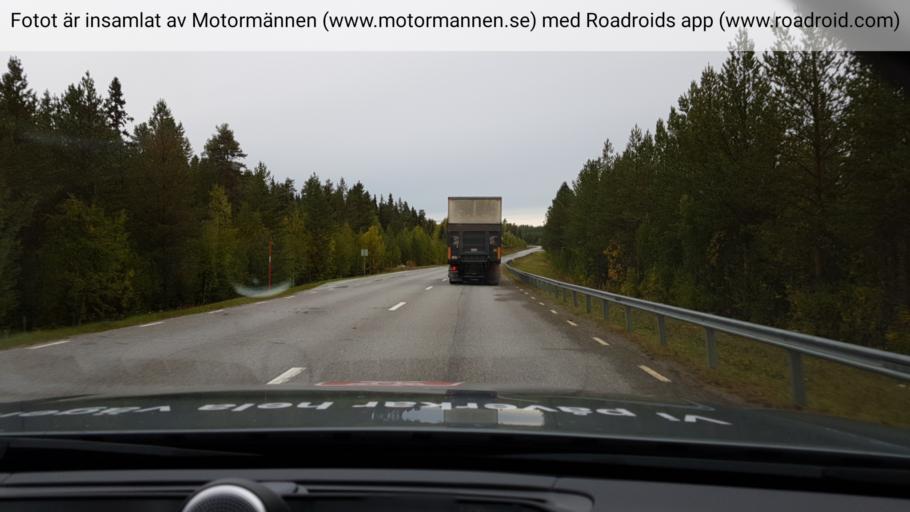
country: SE
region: Jaemtland
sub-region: Stroemsunds Kommun
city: Stroemsund
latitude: 64.2392
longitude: 15.4537
